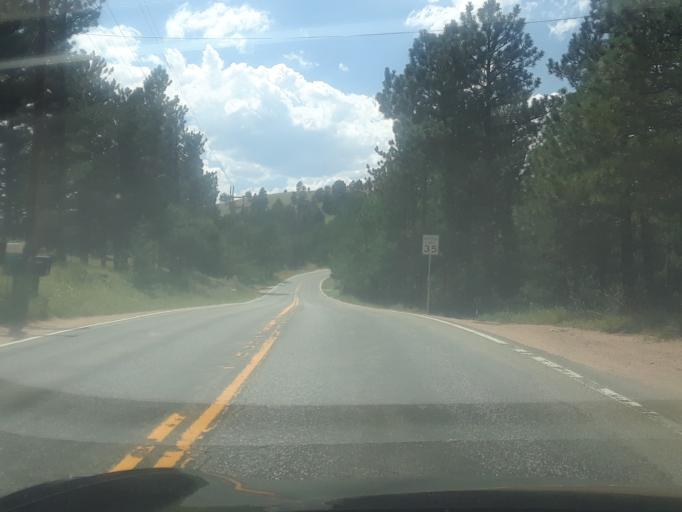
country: US
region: Colorado
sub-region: Boulder County
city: Boulder
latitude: 40.0485
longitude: -105.3363
